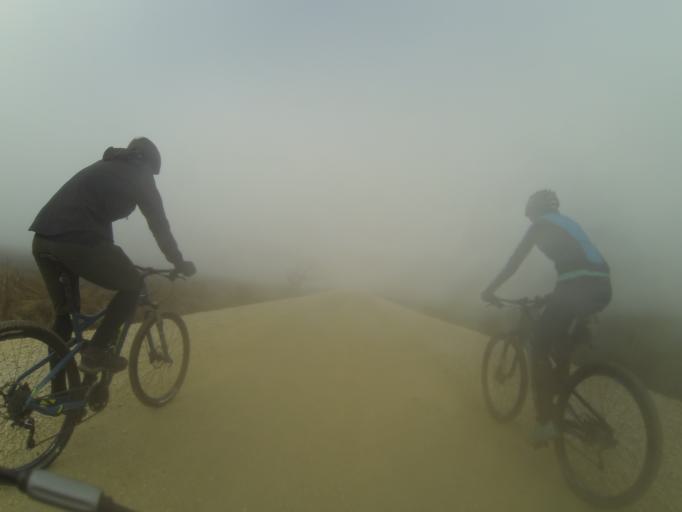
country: RO
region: Mehedinti
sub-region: Comuna Baclesu
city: Baclesu
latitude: 44.4554
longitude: 23.1176
